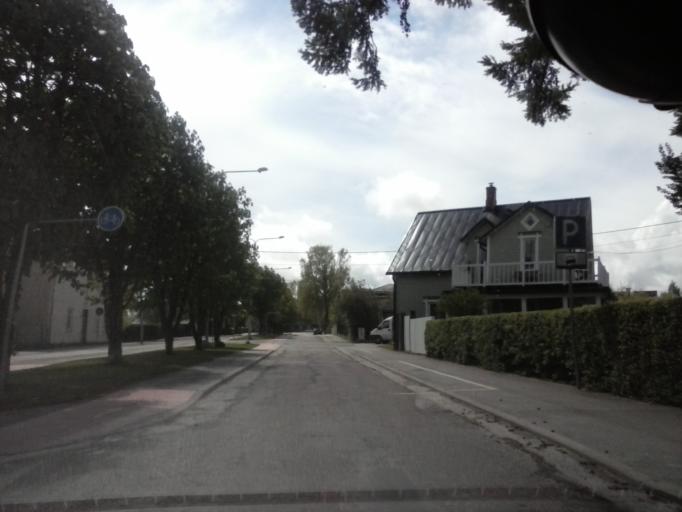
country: EE
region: Tartu
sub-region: Tartu linn
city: Tartu
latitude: 58.3635
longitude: 26.7256
